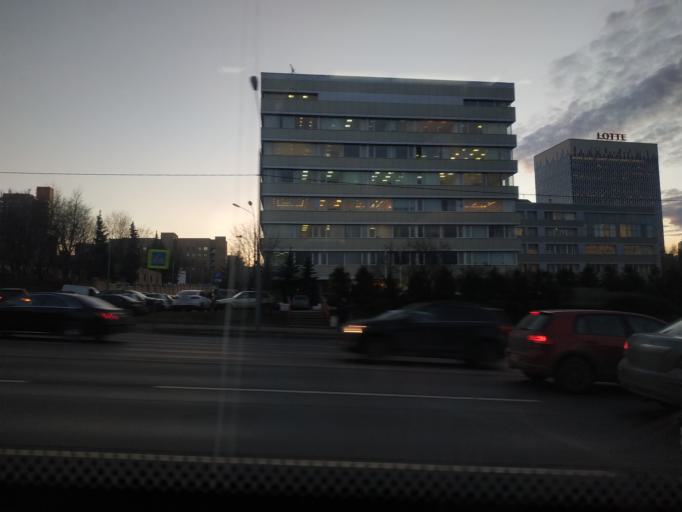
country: RU
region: Moskovskaya
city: Cheremushki
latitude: 55.6542
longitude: 37.5432
